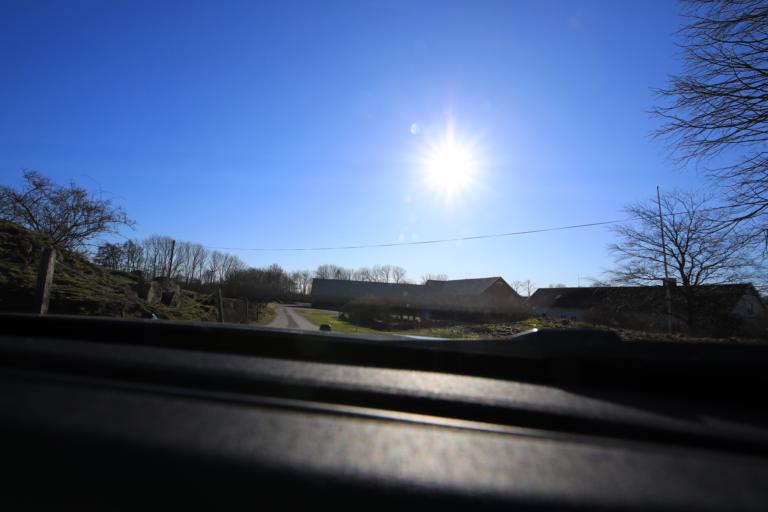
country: SE
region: Halland
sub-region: Varbergs Kommun
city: Tvaaker
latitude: 57.0527
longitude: 12.3763
